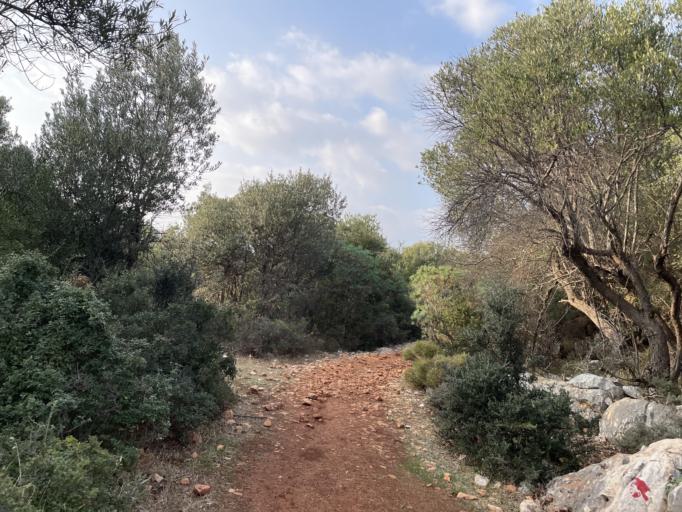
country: TR
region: Antalya
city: Kas
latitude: 36.1614
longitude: 29.6556
